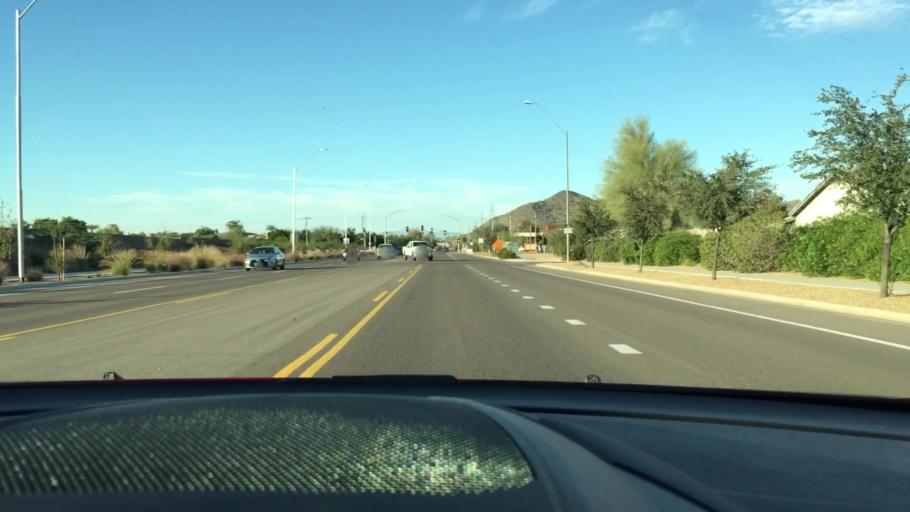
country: US
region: Arizona
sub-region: Maricopa County
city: Sun City West
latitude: 33.6942
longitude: -112.2551
